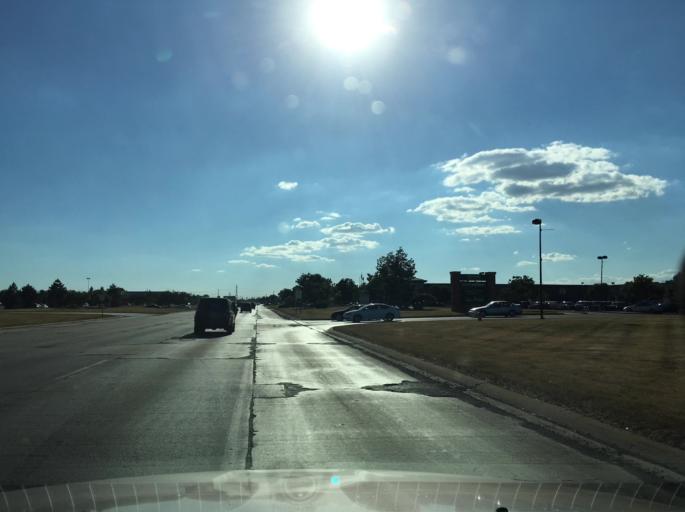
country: US
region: Michigan
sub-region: Macomb County
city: Utica
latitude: 42.6277
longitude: -82.9849
